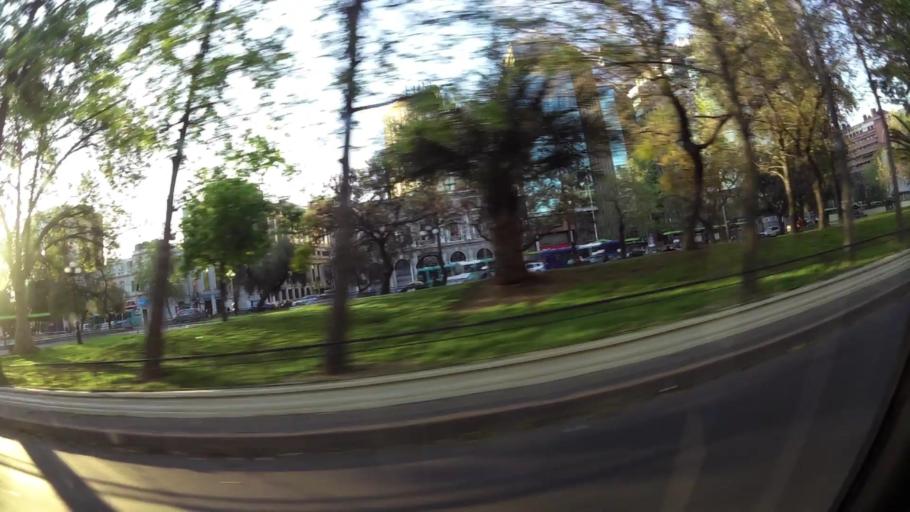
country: CL
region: Santiago Metropolitan
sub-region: Provincia de Santiago
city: Santiago
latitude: -33.4456
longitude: -70.6567
